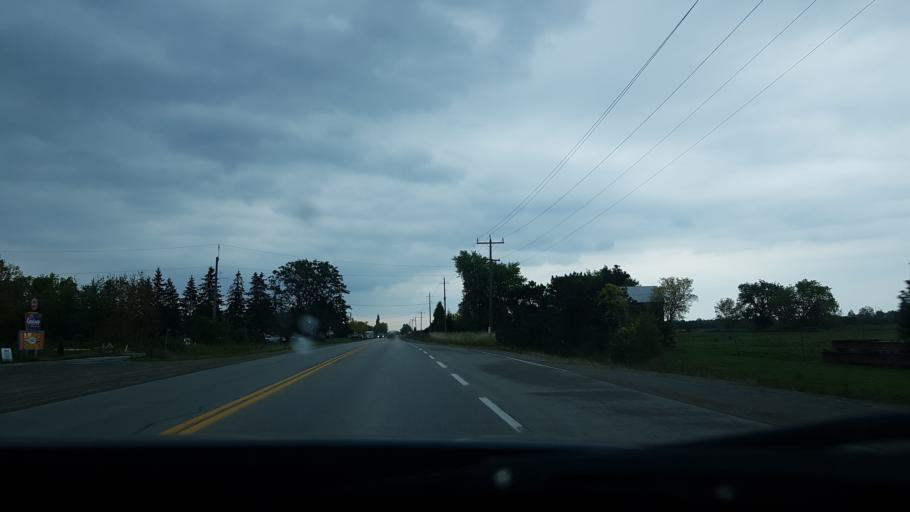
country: CA
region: Ontario
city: Omemee
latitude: 44.3653
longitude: -78.6929
